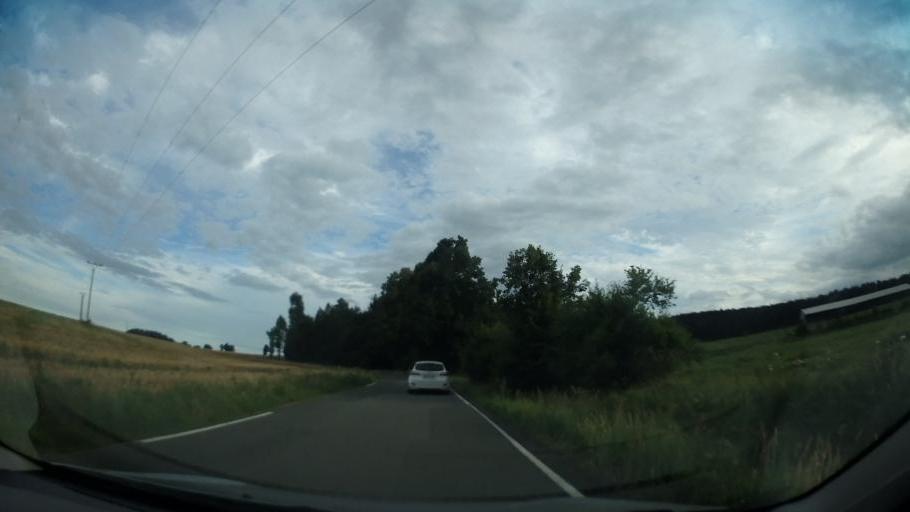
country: CZ
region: Olomoucky
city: Horni Stepanov
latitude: 49.5587
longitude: 16.7666
